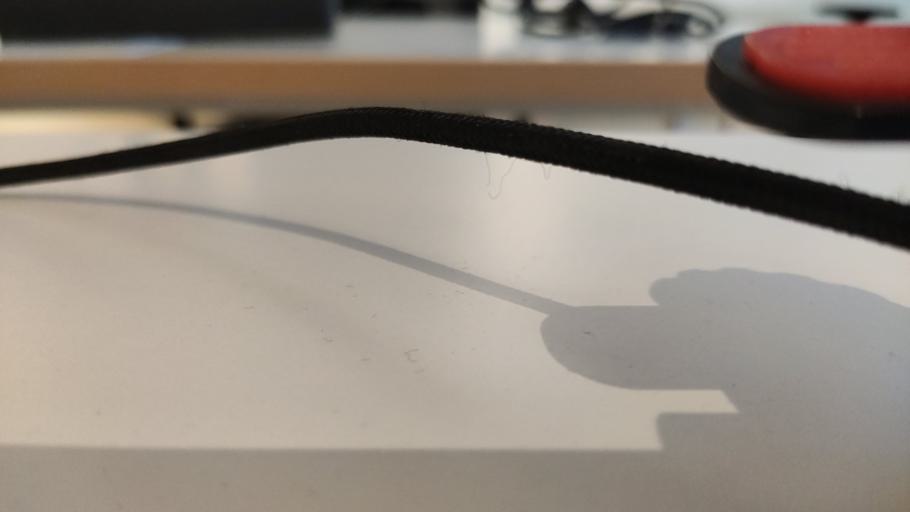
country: RU
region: Moskovskaya
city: Ruza
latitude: 55.8010
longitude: 36.2898
